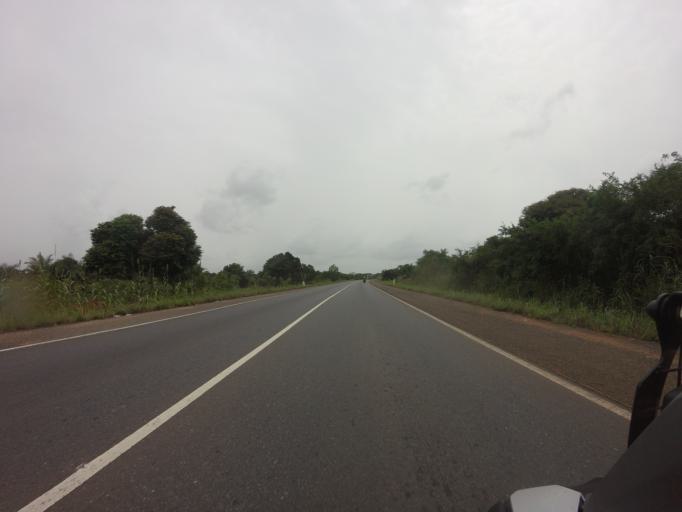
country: GH
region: Volta
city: Keta
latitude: 6.1144
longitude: 0.8010
